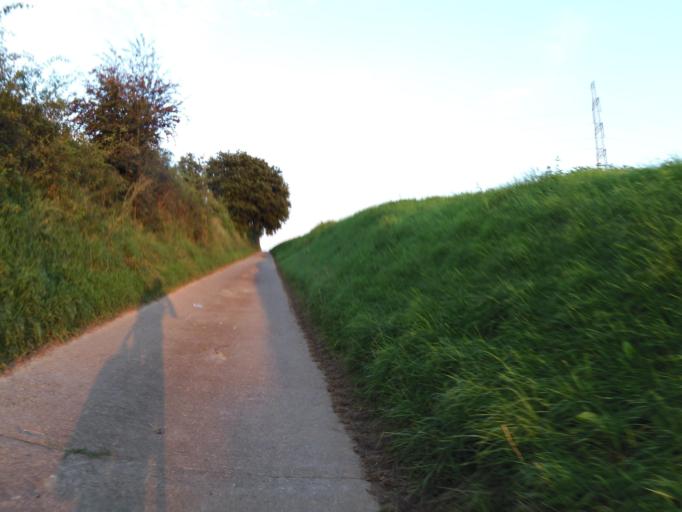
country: BE
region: Wallonia
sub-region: Province de Liege
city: Juprelle
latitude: 50.7631
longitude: 5.5356
